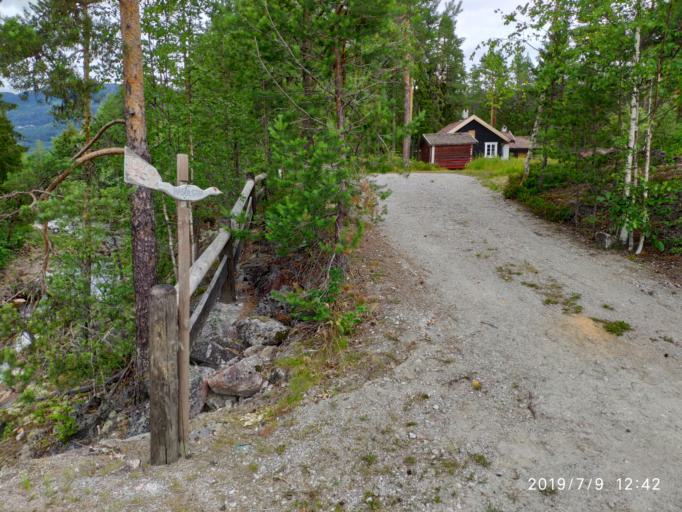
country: NO
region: Buskerud
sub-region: Fla
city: Fla
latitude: 60.2308
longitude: 9.3603
